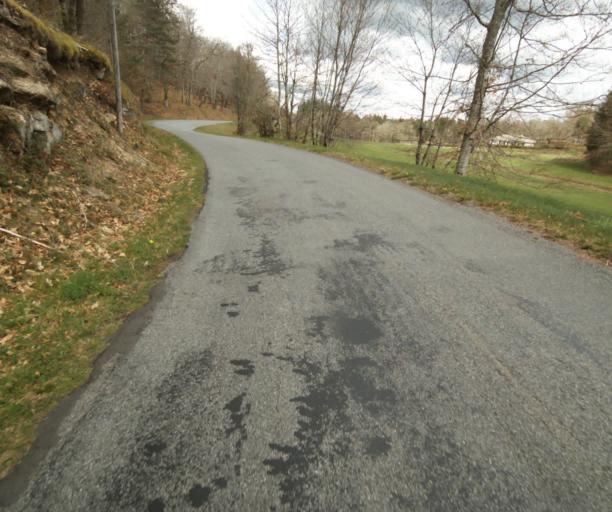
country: FR
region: Limousin
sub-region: Departement de la Correze
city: Correze
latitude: 45.3259
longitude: 1.9545
